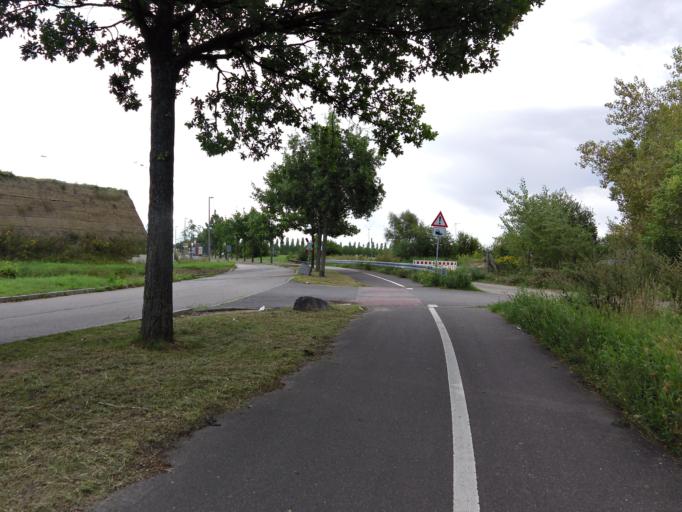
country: DE
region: Saxony
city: Rackwitz
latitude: 51.3886
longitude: 12.4110
